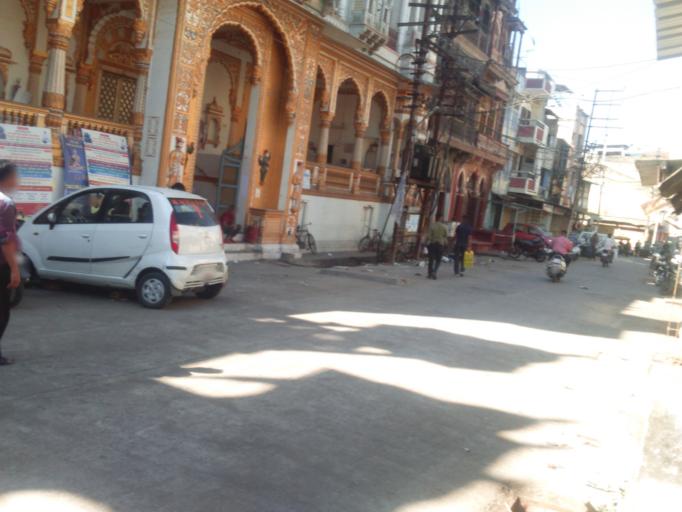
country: IN
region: Madhya Pradesh
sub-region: Indore
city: Indore
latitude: 22.7186
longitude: 75.8511
